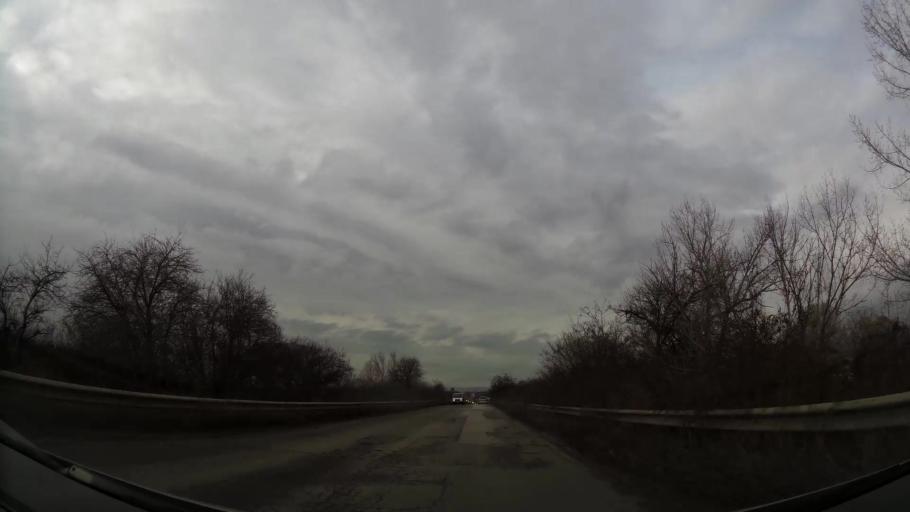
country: BG
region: Sofia-Capital
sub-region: Stolichna Obshtina
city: Sofia
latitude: 42.7497
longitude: 23.2772
